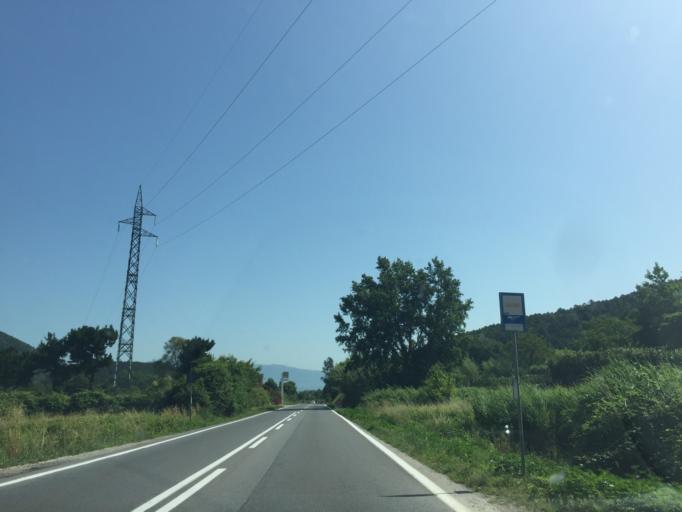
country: IT
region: Tuscany
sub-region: Province of Pisa
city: Asciano
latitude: 43.7853
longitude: 10.4681
